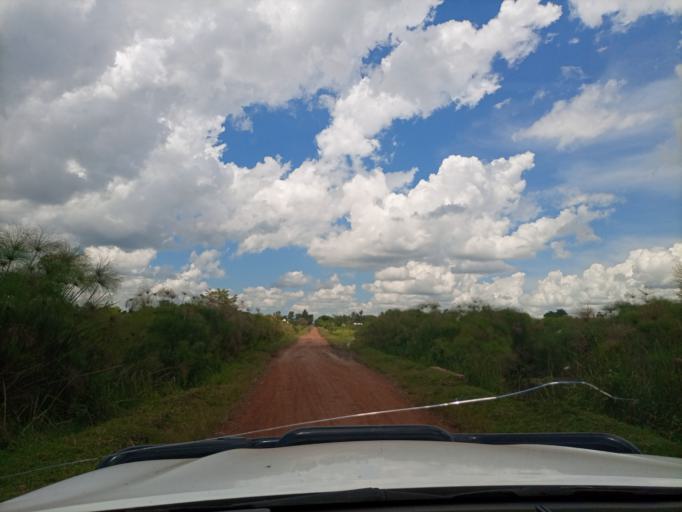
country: UG
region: Eastern Region
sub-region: Busia District
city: Busia
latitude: 0.6351
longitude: 33.9925
